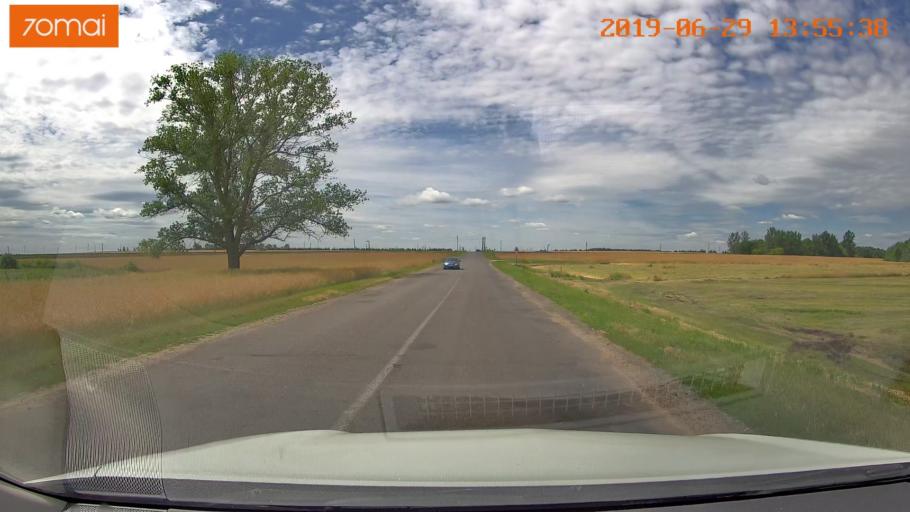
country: BY
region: Minsk
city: Slutsk
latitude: 52.9844
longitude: 27.5159
